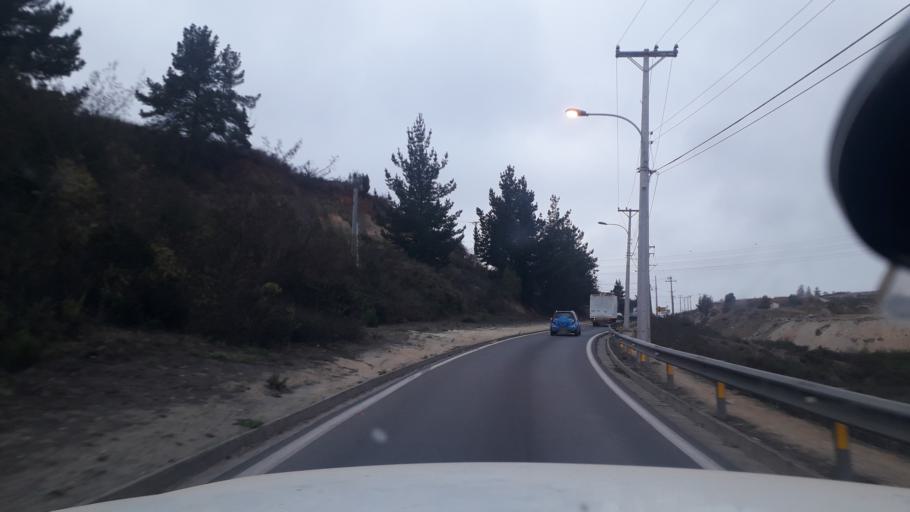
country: CL
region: Valparaiso
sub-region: Provincia de Valparaiso
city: Vina del Mar
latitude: -33.0777
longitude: -71.5468
